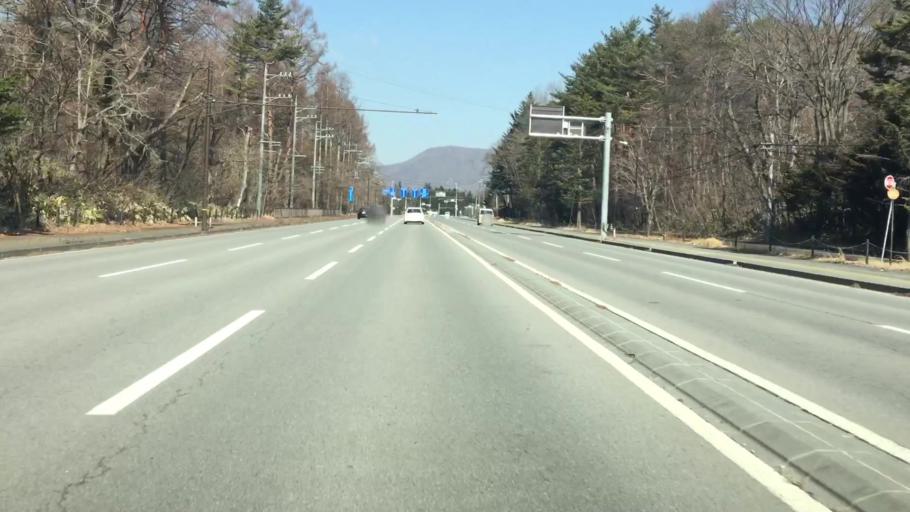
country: JP
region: Nagano
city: Saku
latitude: 36.3212
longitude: 138.6299
